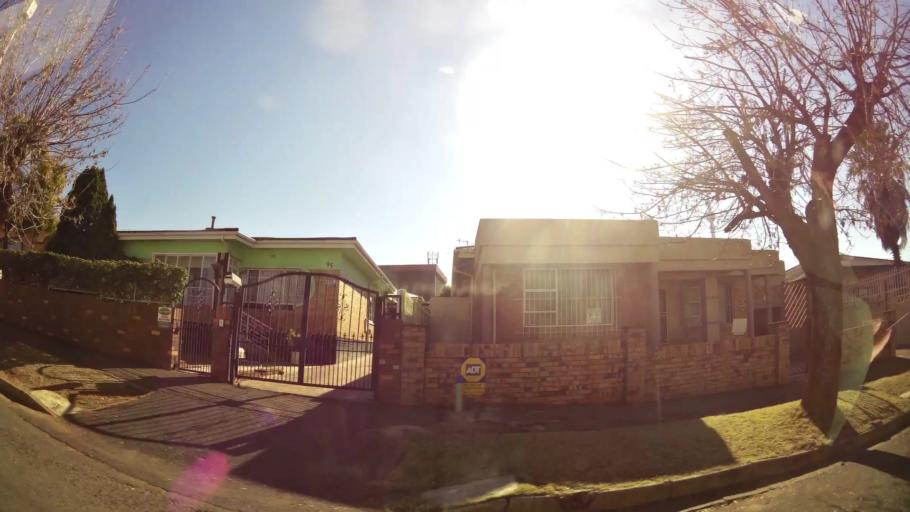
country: ZA
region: Gauteng
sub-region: City of Johannesburg Metropolitan Municipality
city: Johannesburg
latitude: -26.1965
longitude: 28.0014
